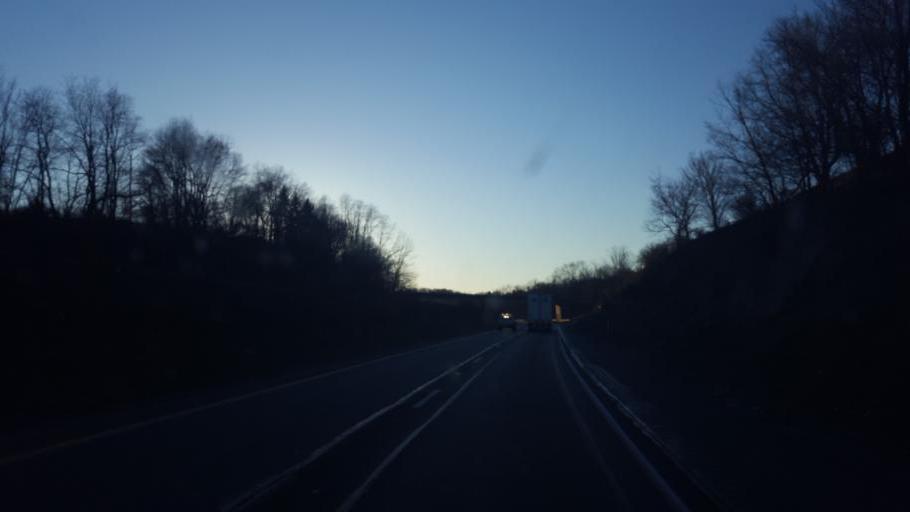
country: US
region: Pennsylvania
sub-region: Washington County
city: Wolfdale
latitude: 40.1245
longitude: -80.3704
